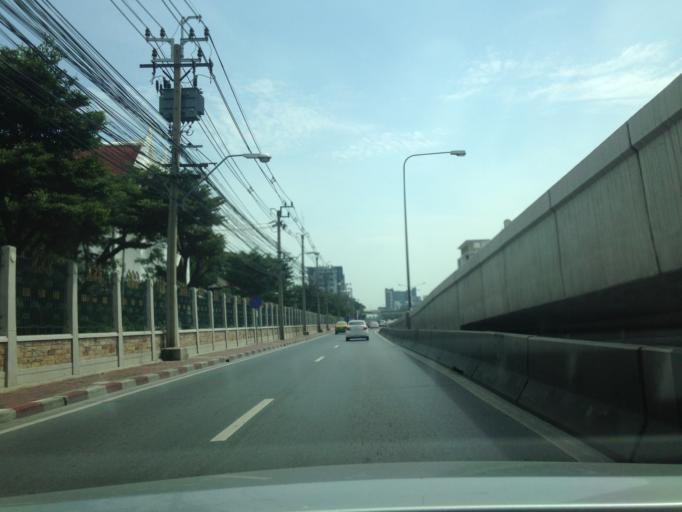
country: TH
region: Bangkok
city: Chatuchak
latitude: 13.8466
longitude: 100.5635
